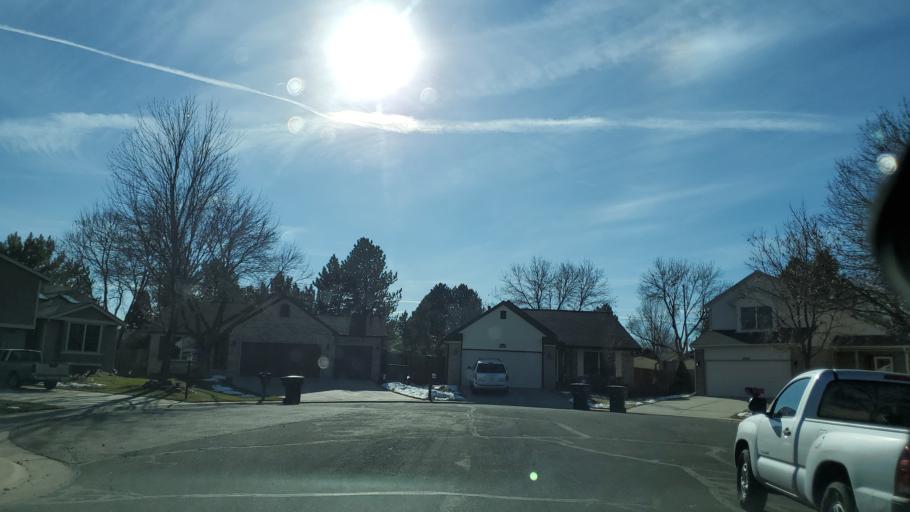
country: US
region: Colorado
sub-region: Adams County
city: Northglenn
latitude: 39.9219
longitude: -104.9565
